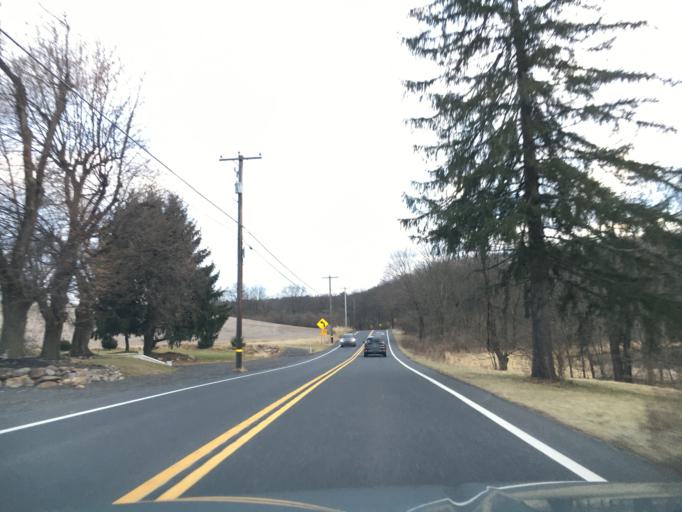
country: US
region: Pennsylvania
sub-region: Lehigh County
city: Schnecksville
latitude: 40.6801
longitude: -75.6520
